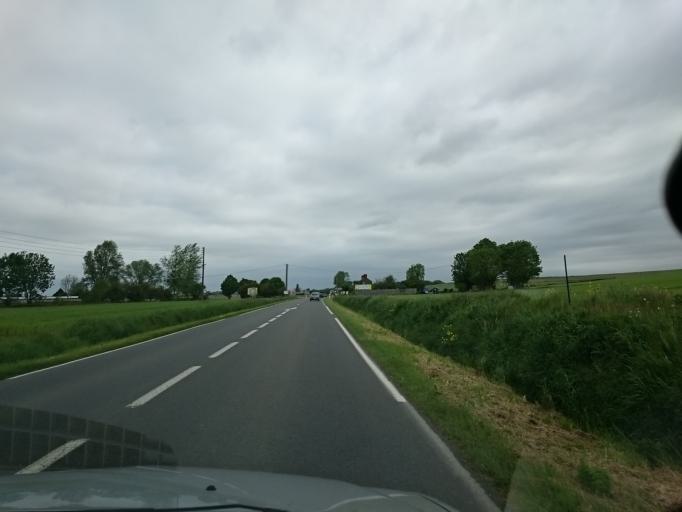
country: FR
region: Lower Normandy
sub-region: Departement de la Manche
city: Pontorson
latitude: 48.5825
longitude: -1.5116
